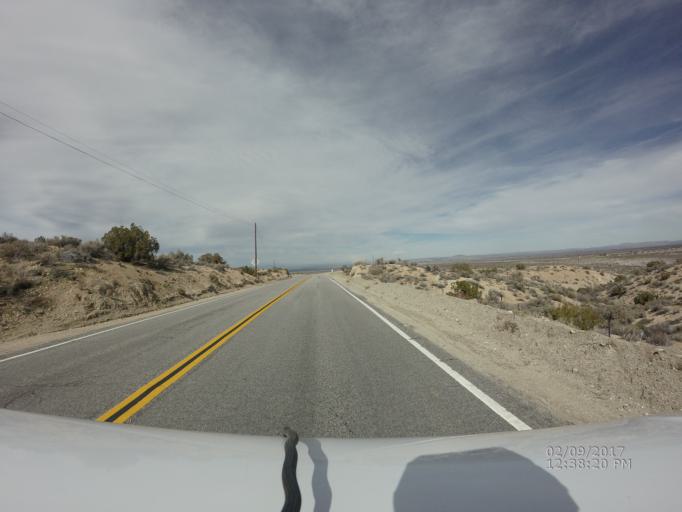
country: US
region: California
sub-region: Los Angeles County
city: Littlerock
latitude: 34.4741
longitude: -117.8607
